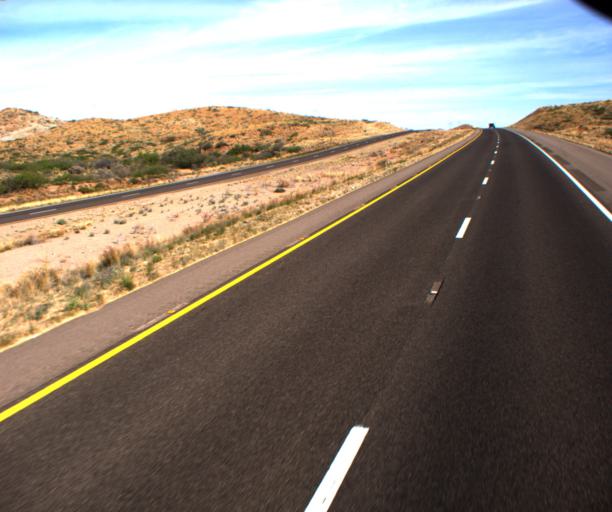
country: US
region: Arizona
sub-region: Cochise County
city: Willcox
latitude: 32.4542
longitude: -109.6645
